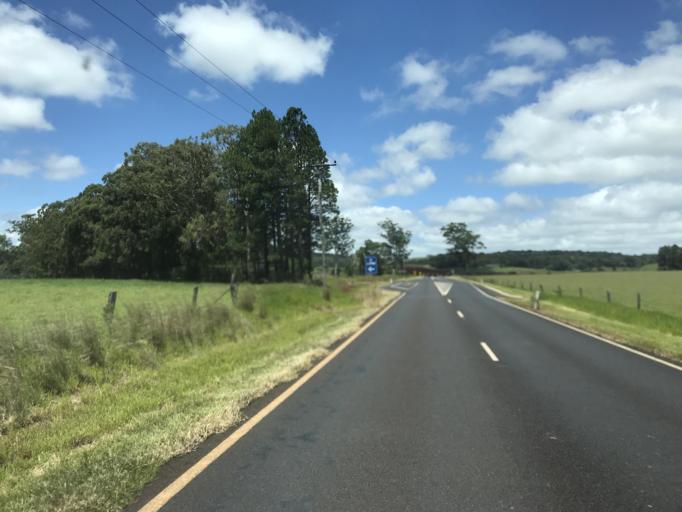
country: AU
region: Queensland
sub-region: Tablelands
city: Ravenshoe
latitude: -17.5100
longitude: 145.4544
